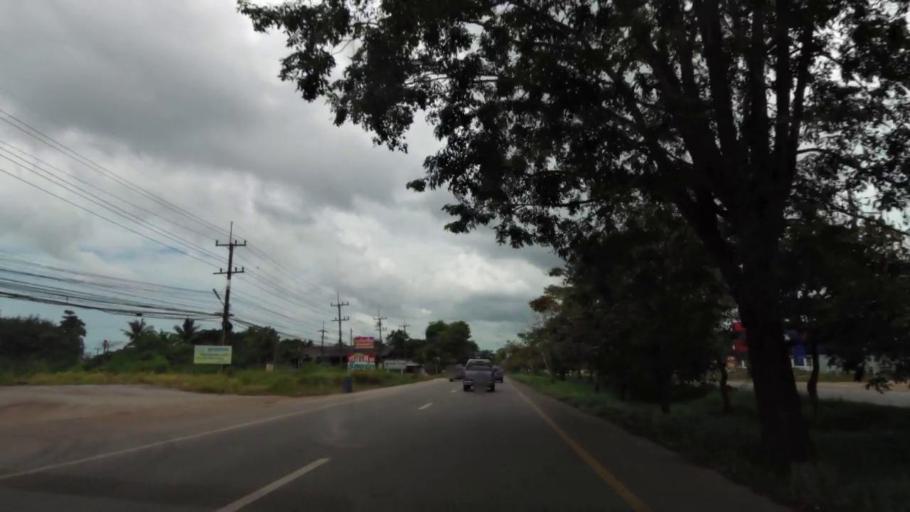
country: TH
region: Rayong
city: Klaeng
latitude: 12.7766
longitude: 101.7197
